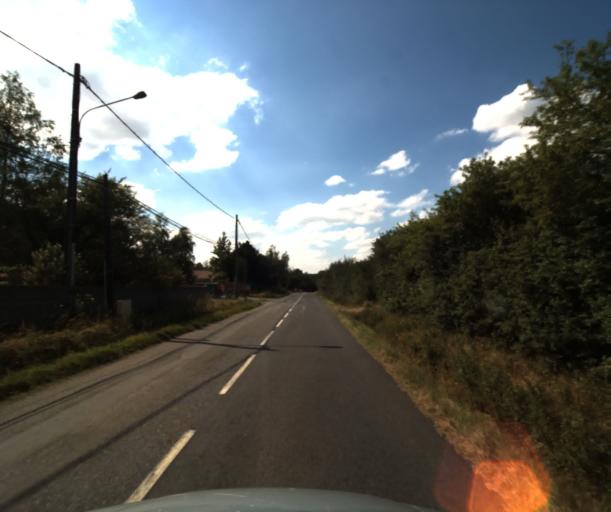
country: FR
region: Midi-Pyrenees
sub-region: Departement de la Haute-Garonne
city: Saint-Lys
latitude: 43.5200
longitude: 1.1659
